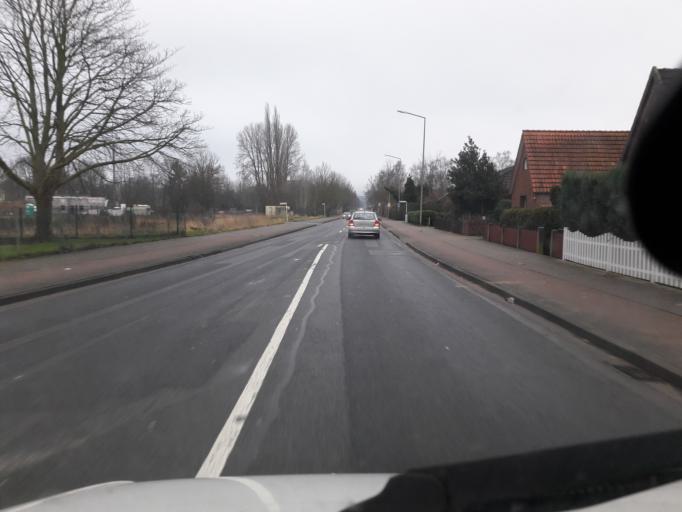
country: DE
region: North Rhine-Westphalia
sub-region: Regierungsbezirk Detmold
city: Minden
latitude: 52.2832
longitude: 8.8871
